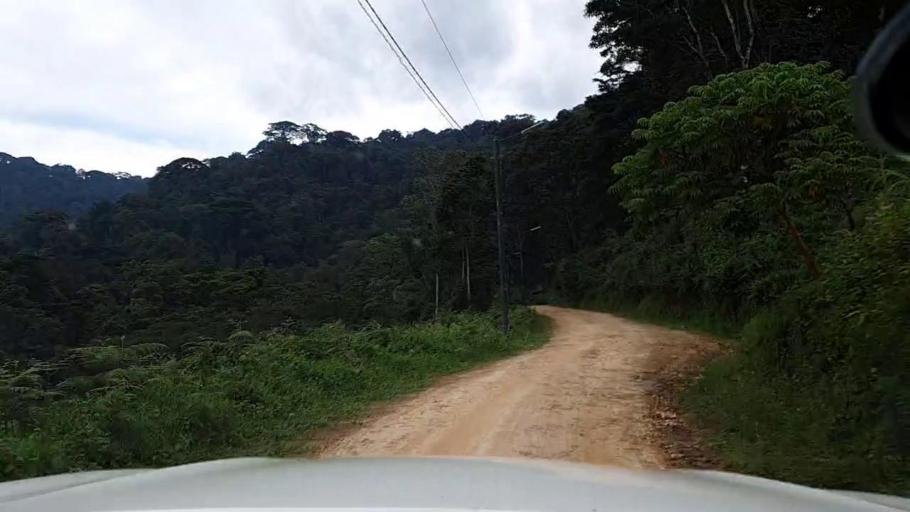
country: RW
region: Western Province
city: Cyangugu
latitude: -2.5678
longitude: 29.2292
